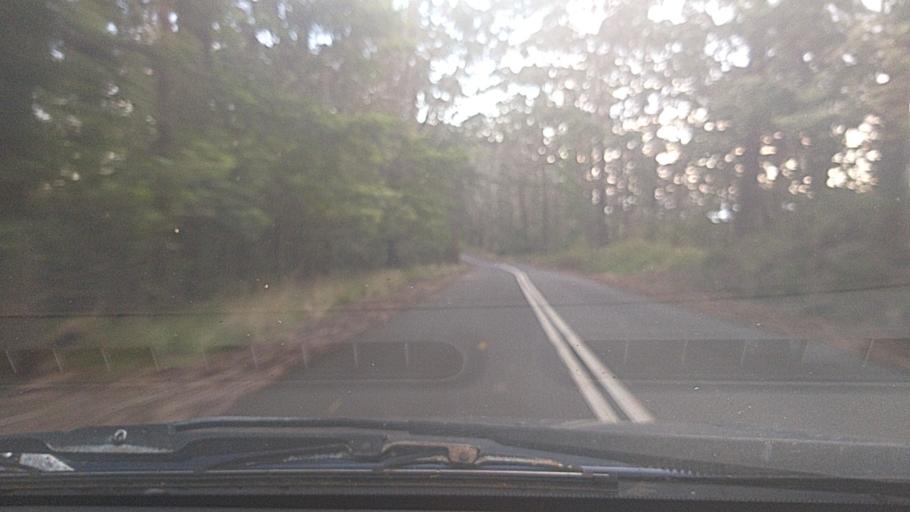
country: AU
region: New South Wales
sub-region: Wollongong
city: Mount Ousley
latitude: -34.3875
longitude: 150.8532
